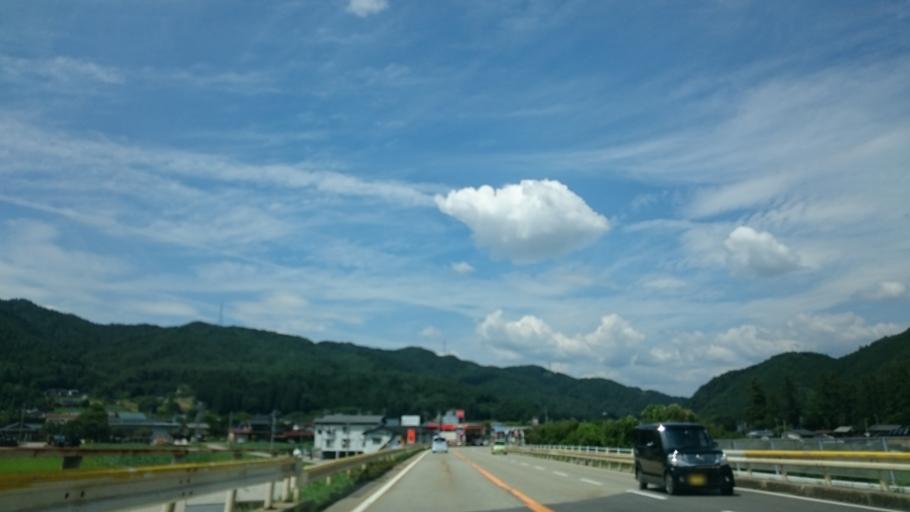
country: JP
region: Gifu
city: Takayama
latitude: 36.0828
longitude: 137.2482
